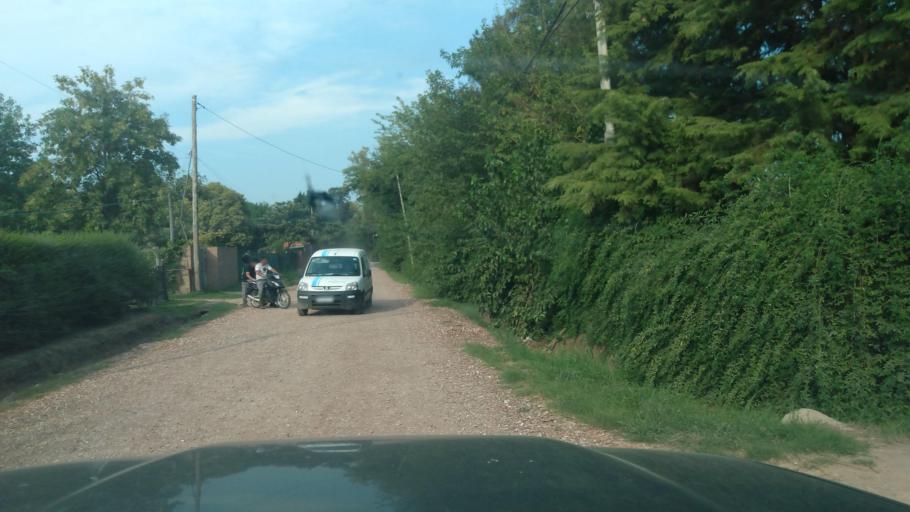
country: AR
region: Buenos Aires
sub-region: Partido de Lujan
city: Lujan
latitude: -34.5484
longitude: -59.1299
